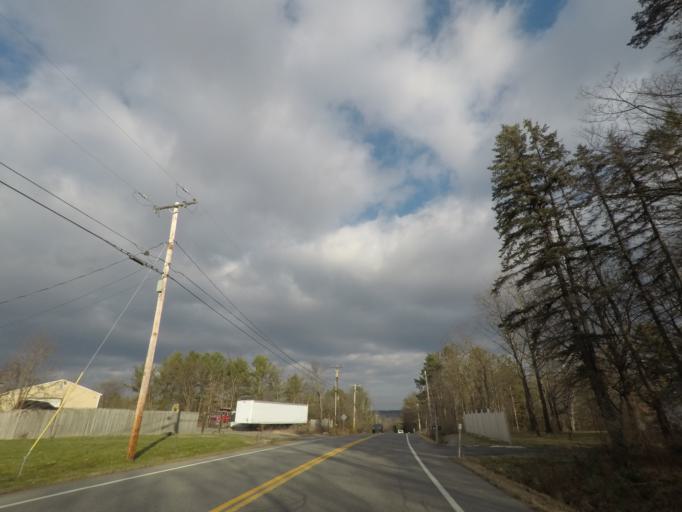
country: US
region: New York
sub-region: Albany County
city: Voorheesville
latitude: 42.6631
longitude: -73.9059
